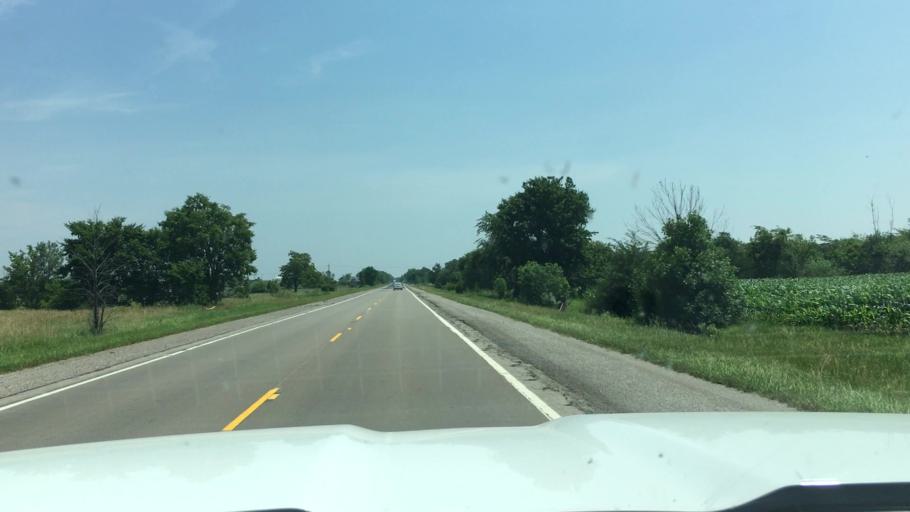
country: US
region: Michigan
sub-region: Saginaw County
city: Chesaning
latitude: 43.1868
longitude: -84.2184
